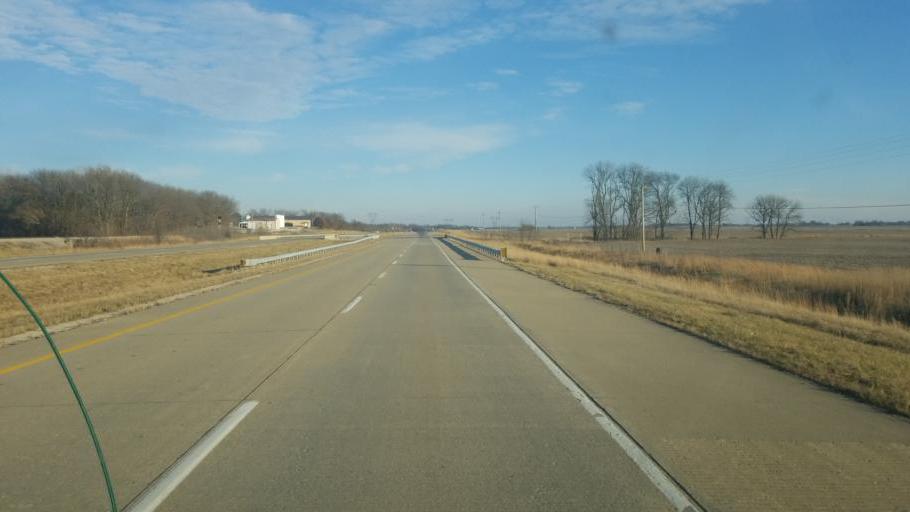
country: US
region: Indiana
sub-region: Knox County
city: Bicknell
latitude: 38.6714
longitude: -87.3517
